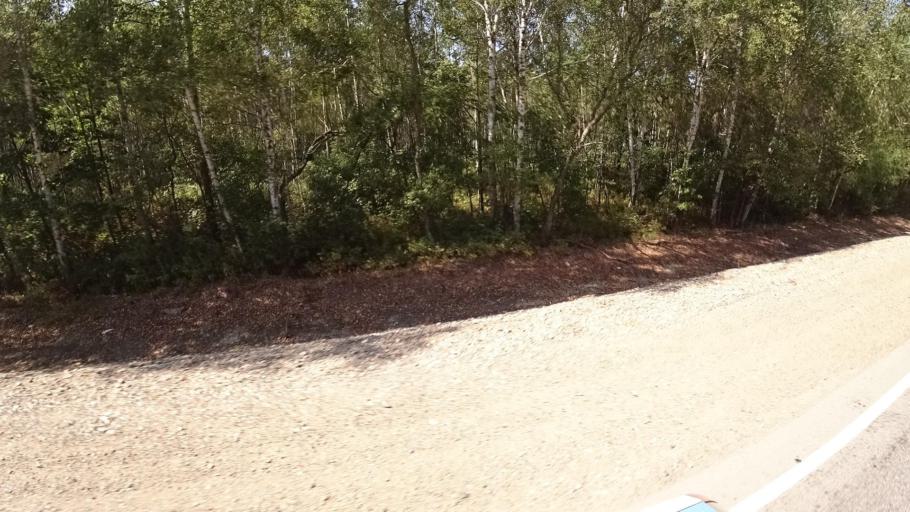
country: RU
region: Khabarovsk Krai
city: Khor
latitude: 47.9881
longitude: 135.0909
